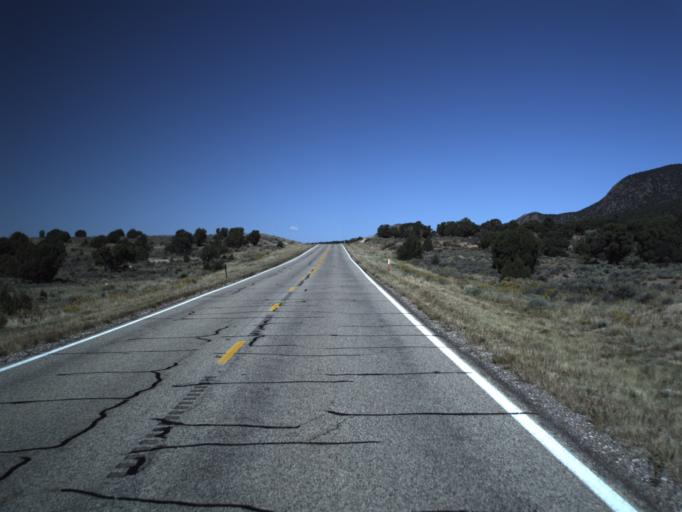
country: US
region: Utah
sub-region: Washington County
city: Enterprise
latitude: 37.6499
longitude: -113.4487
